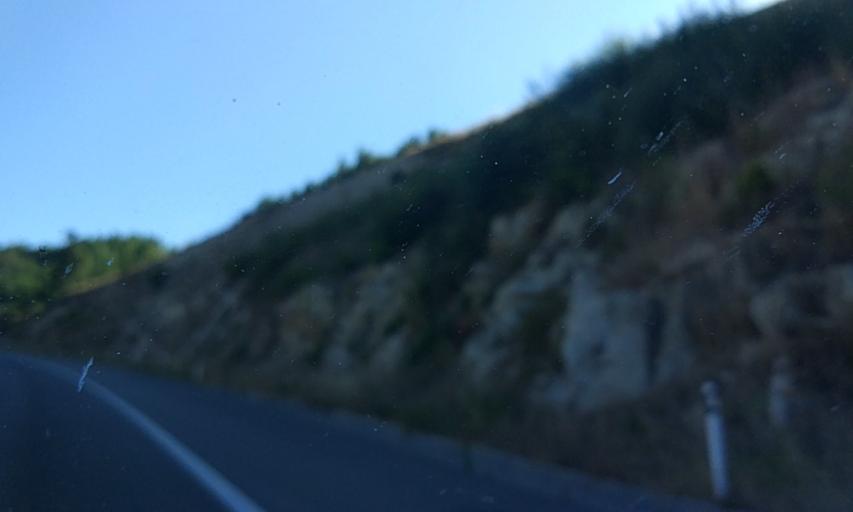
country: PT
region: Vila Real
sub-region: Murca
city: Murca
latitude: 41.3961
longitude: -7.4743
